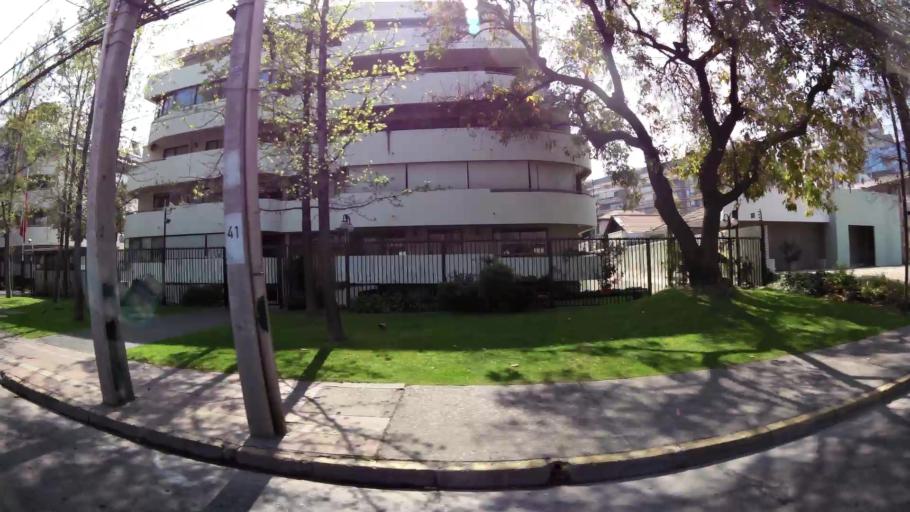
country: CL
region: Santiago Metropolitan
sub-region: Provincia de Santiago
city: Villa Presidente Frei, Nunoa, Santiago, Chile
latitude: -33.3895
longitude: -70.5737
